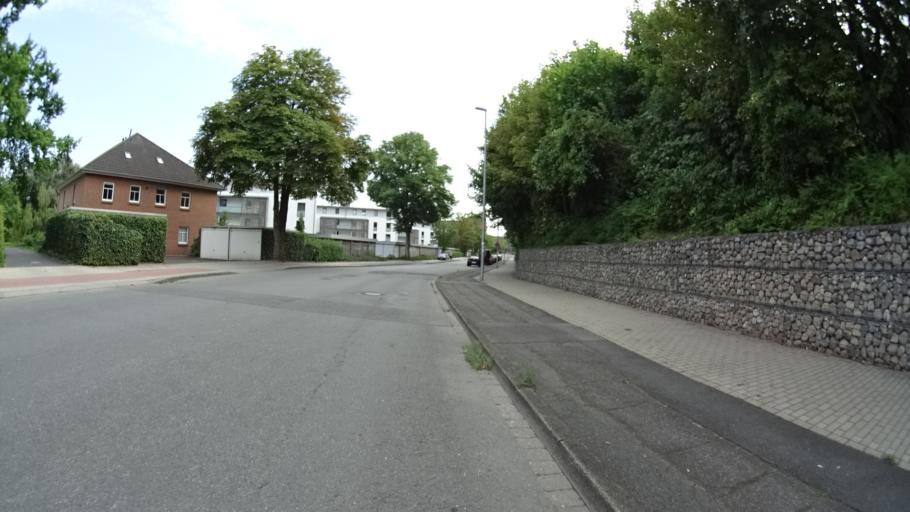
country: DE
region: Lower Saxony
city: Lueneburg
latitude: 53.2573
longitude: 10.4127
